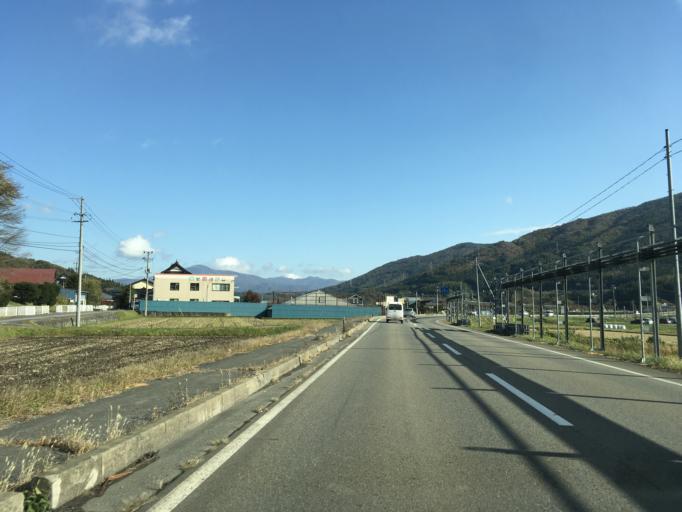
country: JP
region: Iwate
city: Tono
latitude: 39.3314
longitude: 141.4793
